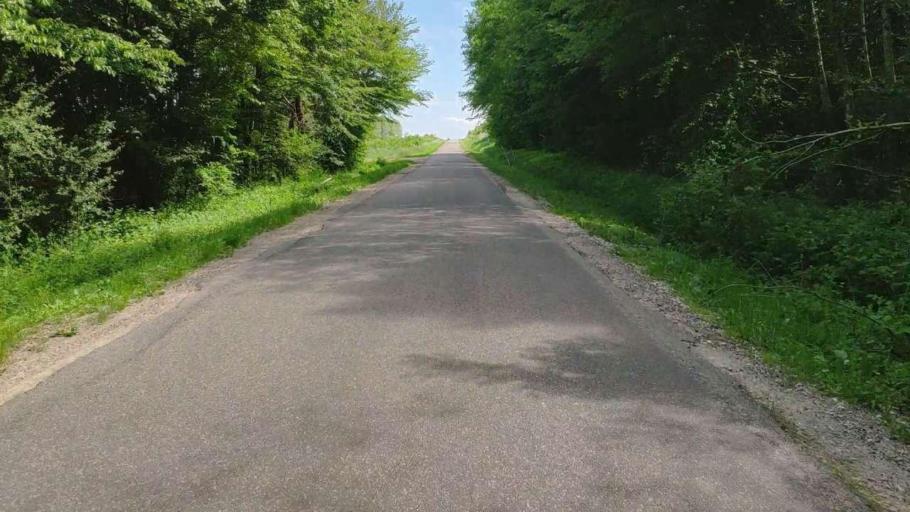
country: FR
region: Franche-Comte
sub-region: Departement du Jura
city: Bletterans
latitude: 46.7137
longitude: 5.4370
